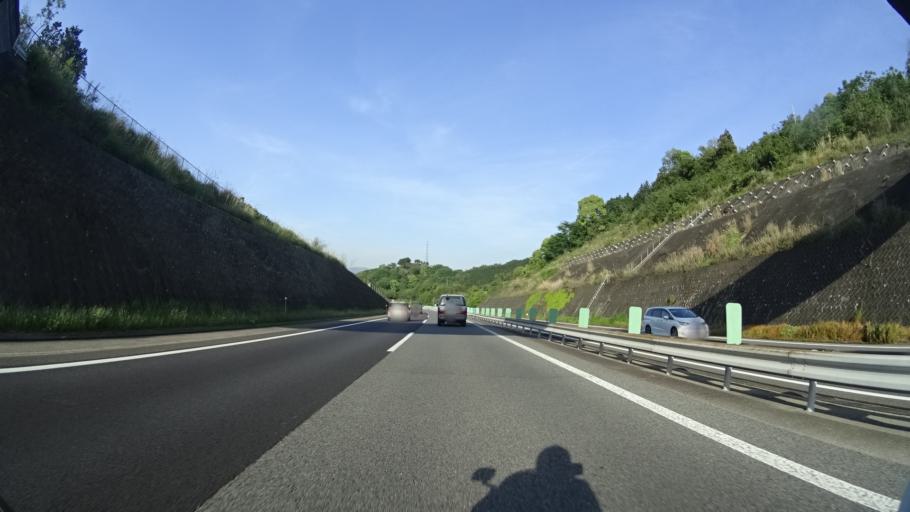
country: JP
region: Ehime
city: Kawanoecho
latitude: 33.9698
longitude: 133.5507
